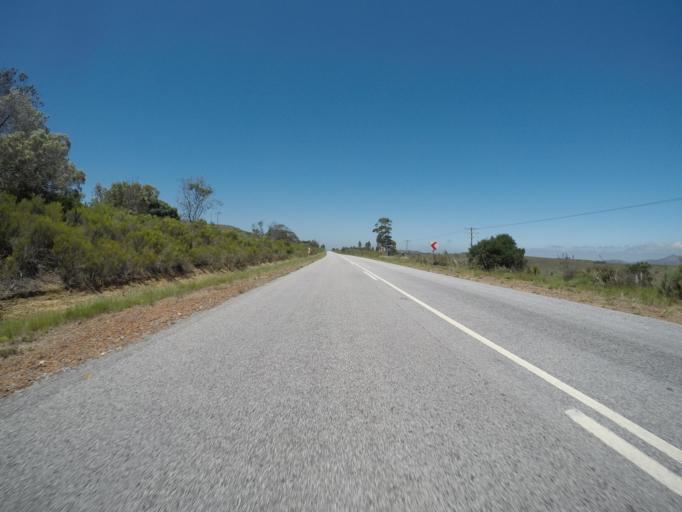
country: ZA
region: Eastern Cape
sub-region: Cacadu District Municipality
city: Kareedouw
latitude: -33.9716
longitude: 24.4674
